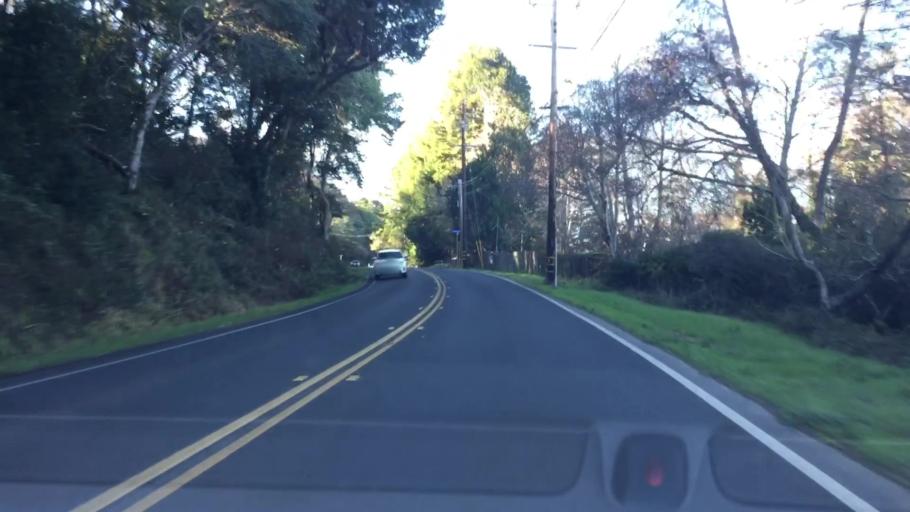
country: US
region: California
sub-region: Marin County
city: Inverness
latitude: 38.0885
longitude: -122.8422
